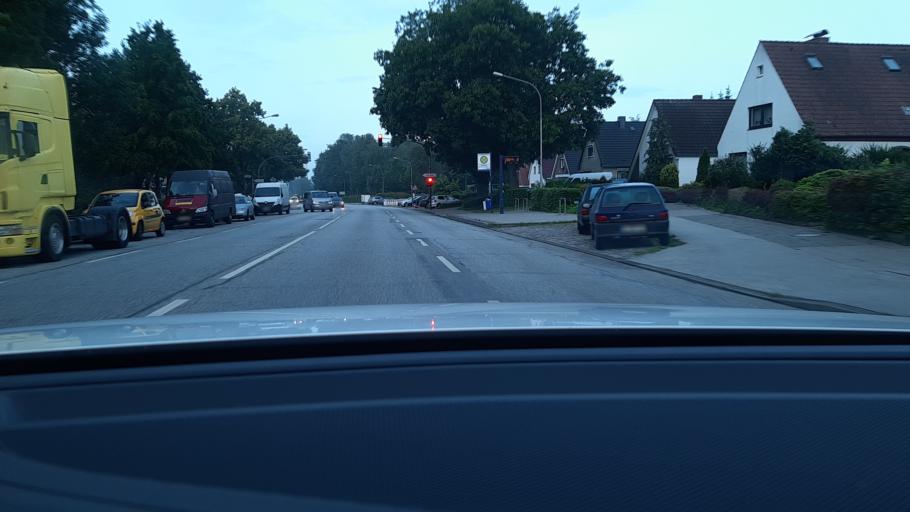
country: DE
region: Schleswig-Holstein
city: Stockelsdorf
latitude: 53.8567
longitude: 10.6411
